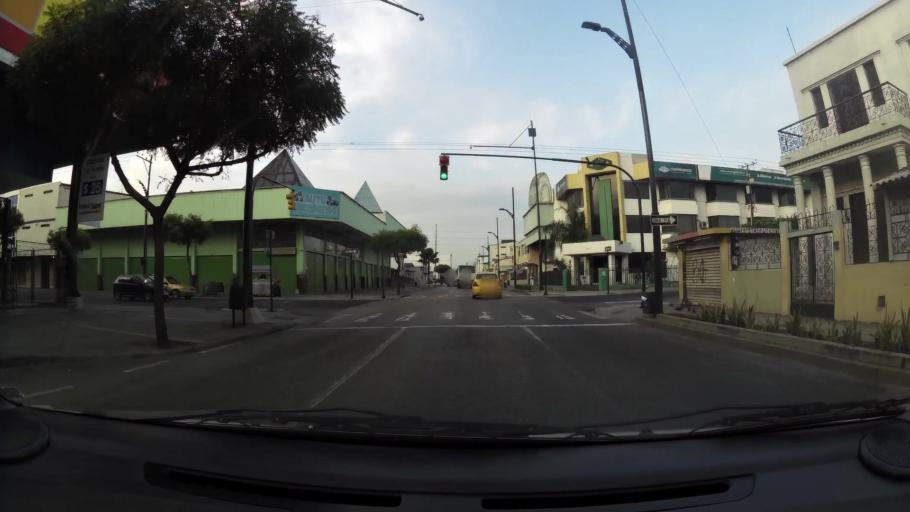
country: EC
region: Guayas
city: Guayaquil
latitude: -2.1908
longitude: -79.8949
